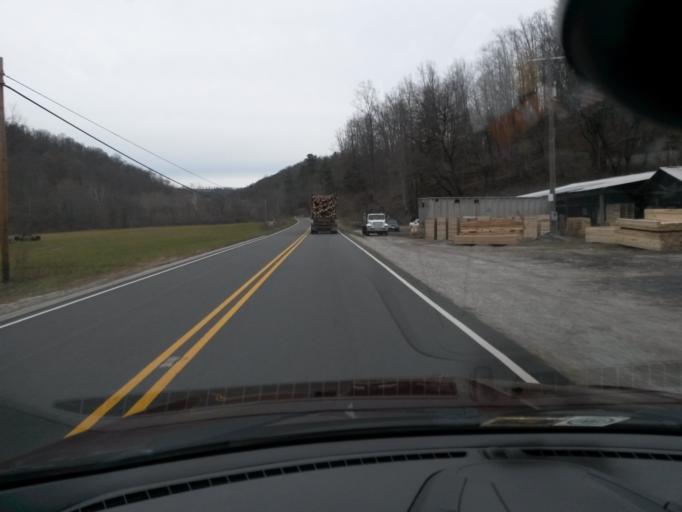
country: US
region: Virginia
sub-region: City of Buena Vista
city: Buena Vista
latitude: 37.6756
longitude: -79.2185
